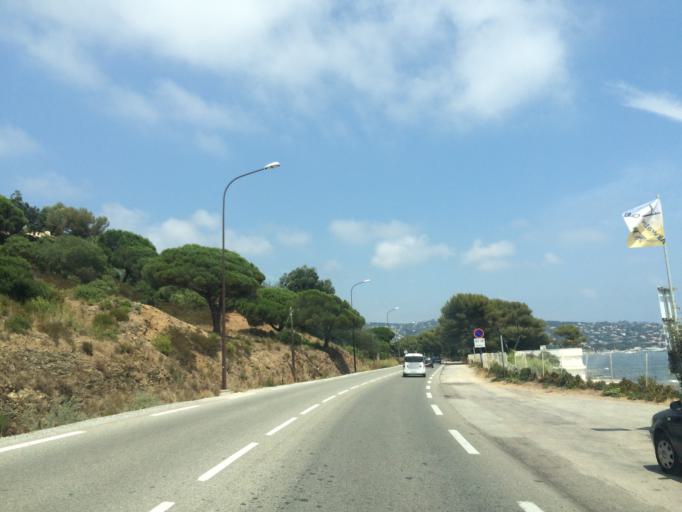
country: FR
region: Provence-Alpes-Cote d'Azur
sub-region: Departement du Var
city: Sainte-Maxime
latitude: 43.3333
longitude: 6.6691
